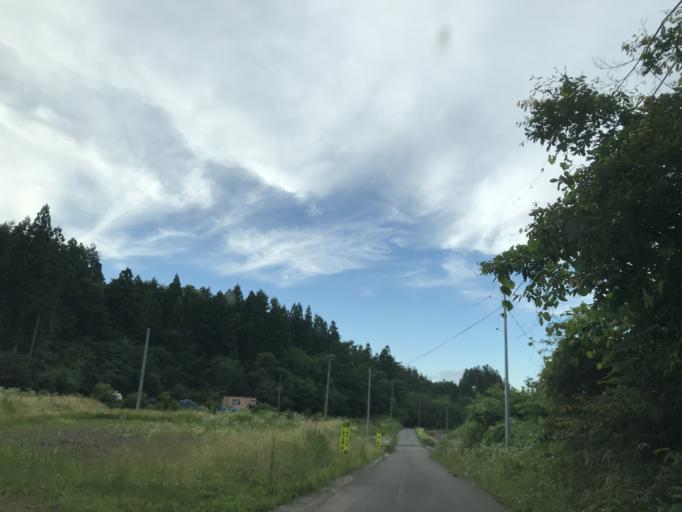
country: JP
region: Iwate
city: Ichinoseki
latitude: 38.9026
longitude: 141.0107
